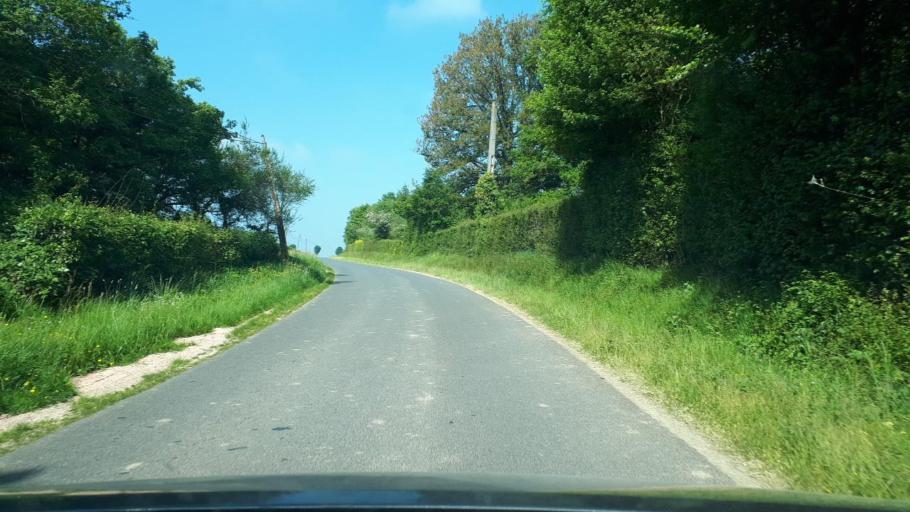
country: FR
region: Centre
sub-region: Departement du Loir-et-Cher
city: Aze
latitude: 47.8535
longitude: 0.9894
